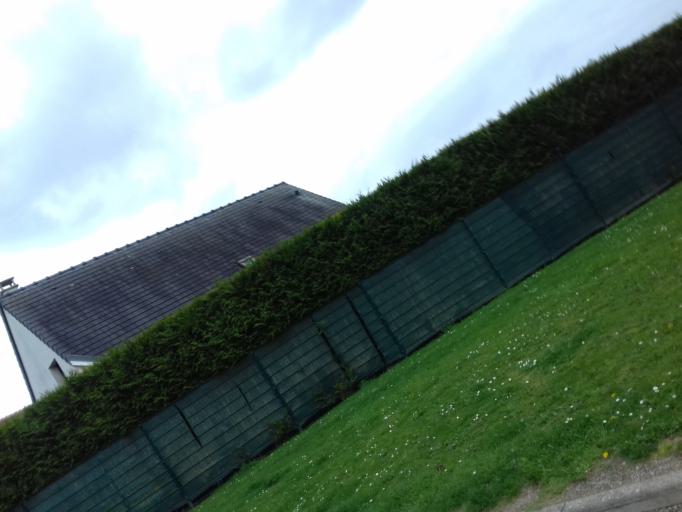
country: FR
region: Picardie
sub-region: Departement de la Somme
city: Longueau
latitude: 49.8736
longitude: 2.3616
